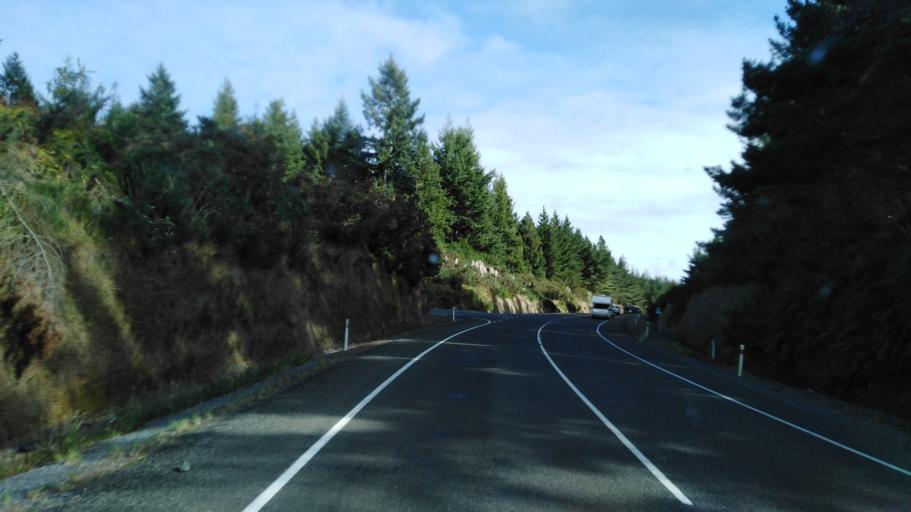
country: NZ
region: Bay of Plenty
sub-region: Rotorua District
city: Rotorua
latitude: -37.9544
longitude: 176.1532
